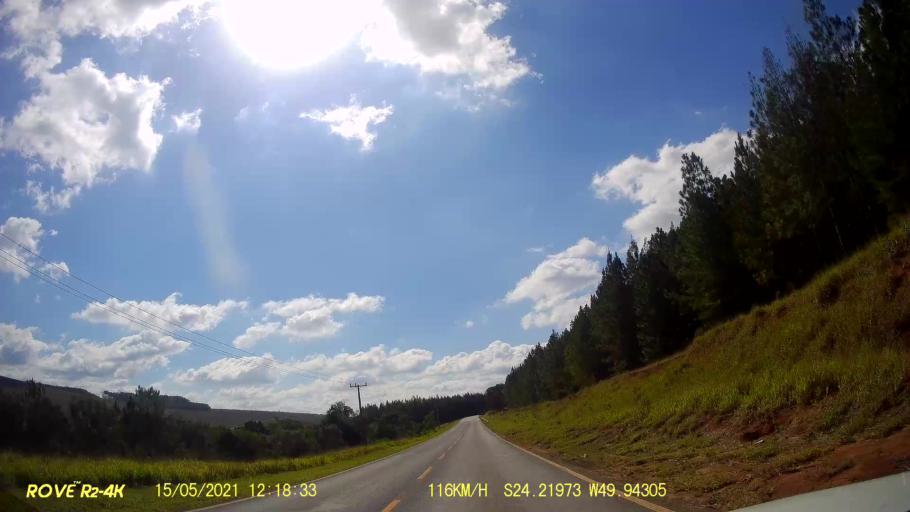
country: BR
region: Parana
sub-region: Jaguariaiva
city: Jaguariaiva
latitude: -24.2195
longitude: -49.9429
